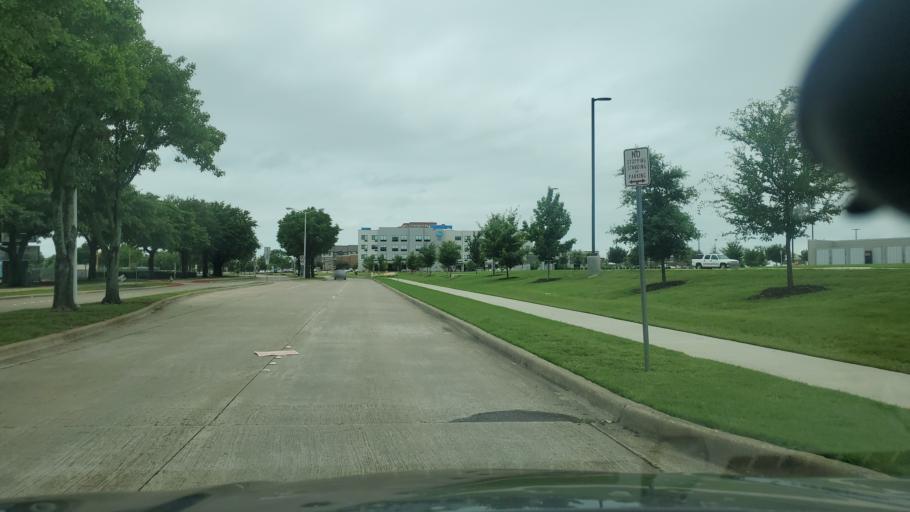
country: US
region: Texas
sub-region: Dallas County
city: Sachse
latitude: 32.9588
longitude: -96.6370
